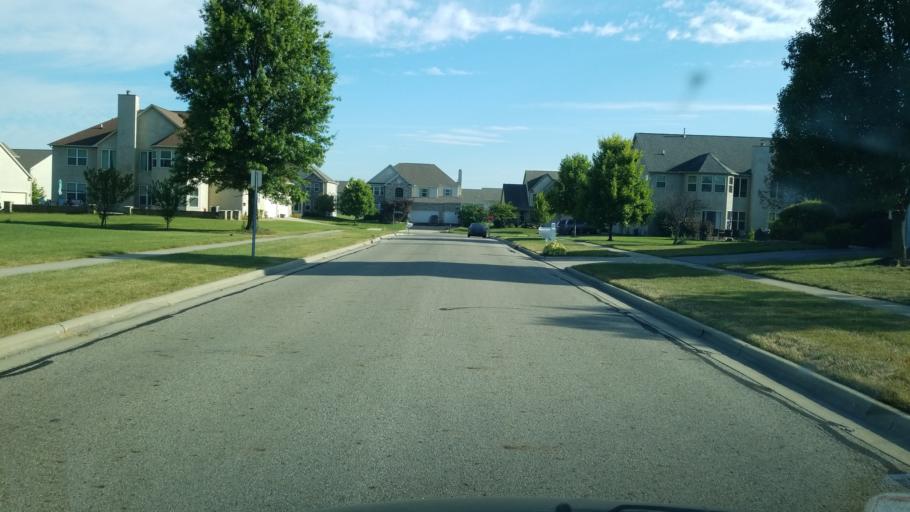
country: US
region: Ohio
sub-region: Delaware County
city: Lewis Center
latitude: 40.1845
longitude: -82.9971
